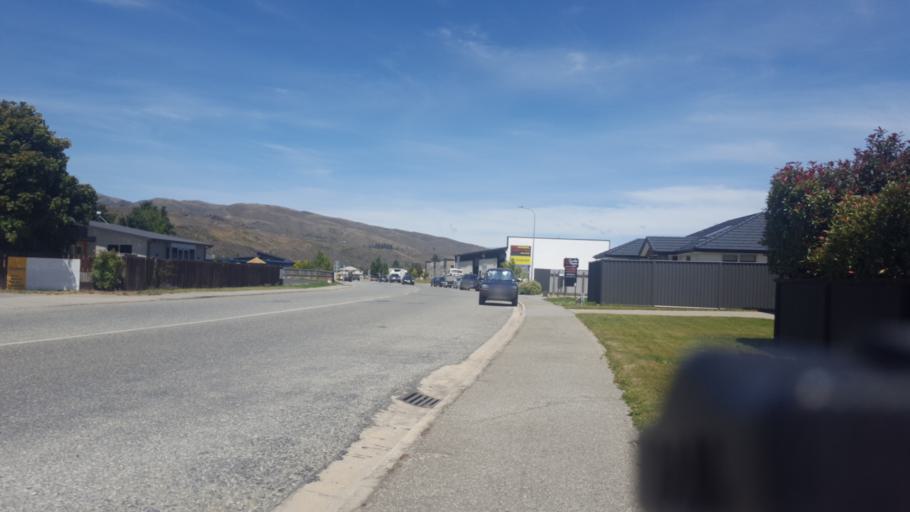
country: NZ
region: Otago
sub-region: Queenstown-Lakes District
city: Wanaka
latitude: -45.0482
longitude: 169.1946
